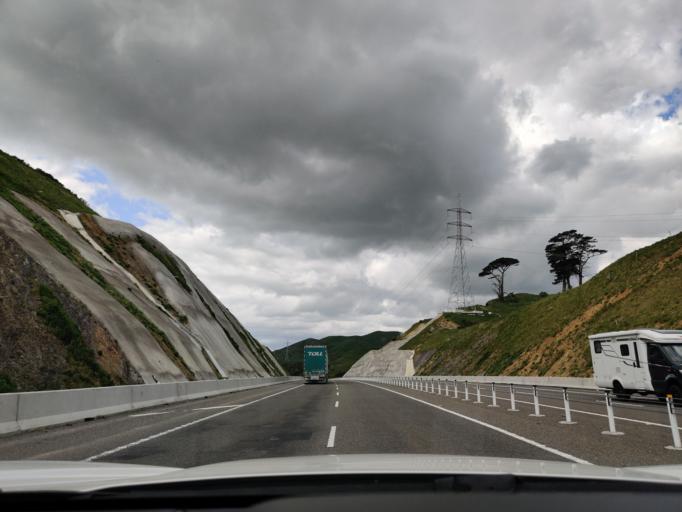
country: NZ
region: Wellington
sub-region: Porirua City
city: Porirua
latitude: -41.1546
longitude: 174.8777
